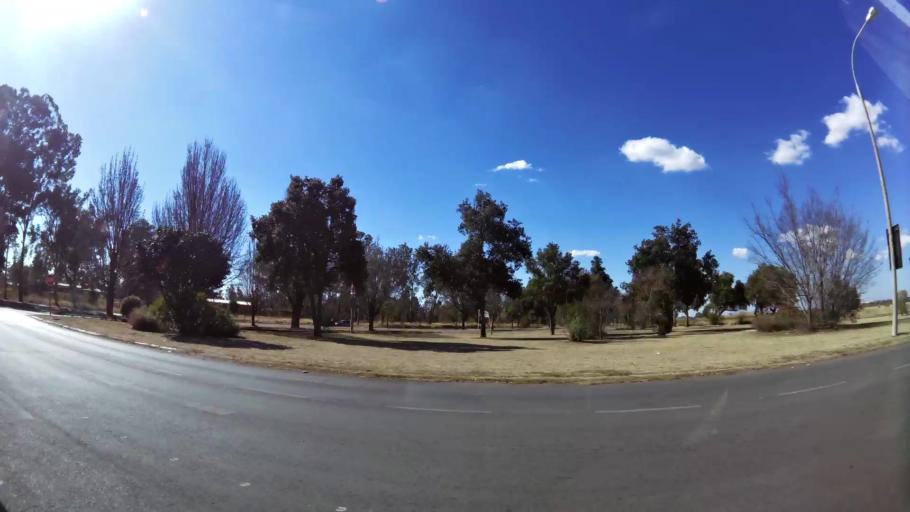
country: ZA
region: Gauteng
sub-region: West Rand District Municipality
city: Carletonville
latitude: -26.3440
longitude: 27.3947
